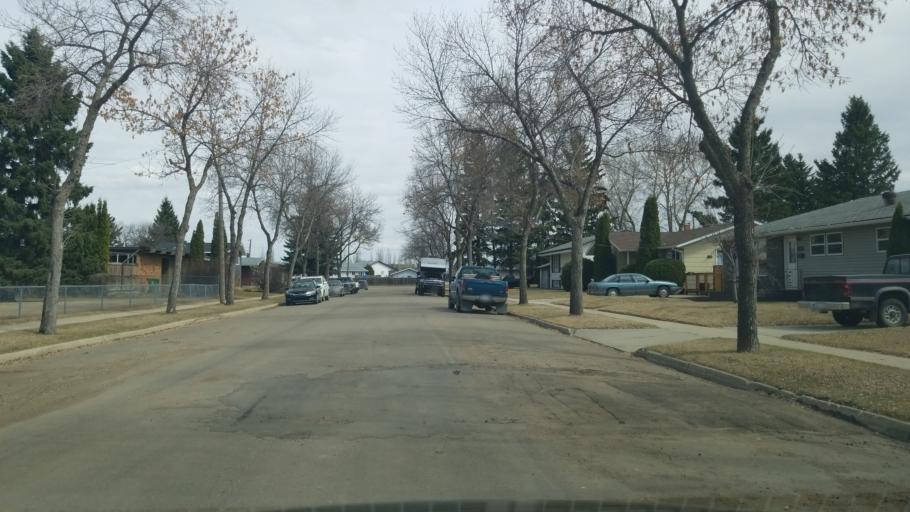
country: CA
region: Saskatchewan
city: Lloydminster
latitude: 53.2725
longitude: -109.9996
